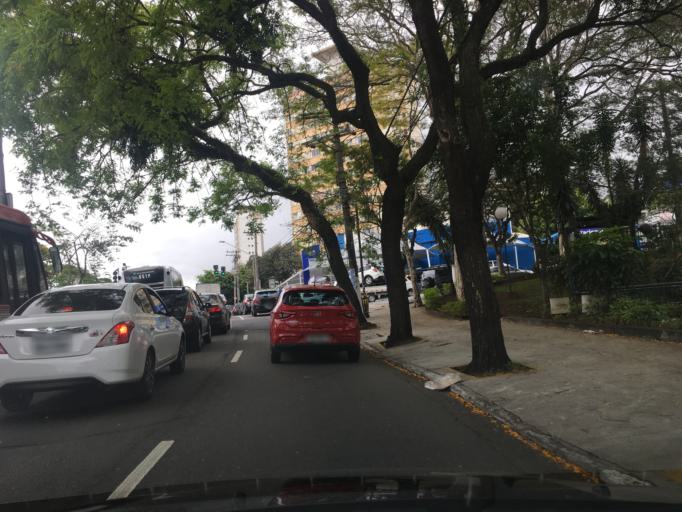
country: BR
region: Sao Paulo
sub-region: Sao Paulo
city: Sao Paulo
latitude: -23.5780
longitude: -46.7083
